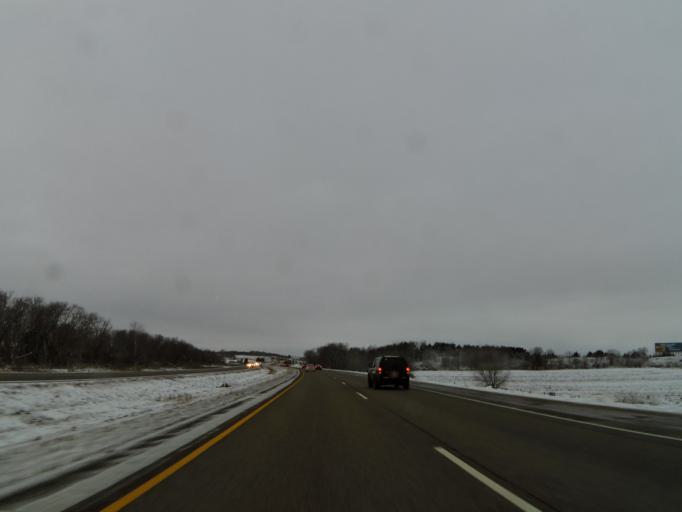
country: US
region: Wisconsin
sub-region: Saint Croix County
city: Hammond
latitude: 44.9434
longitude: -92.4709
